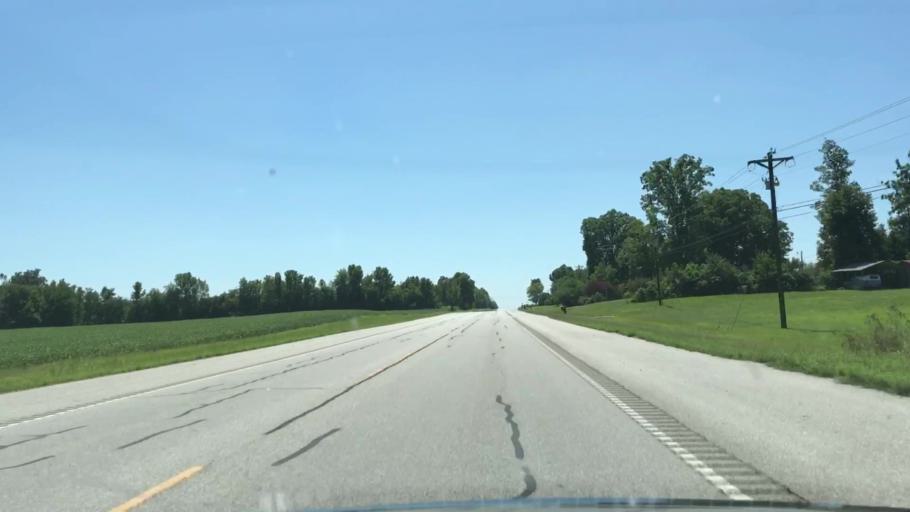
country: US
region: Tennessee
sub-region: Putnam County
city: Baxter
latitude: 36.1853
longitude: -85.6221
